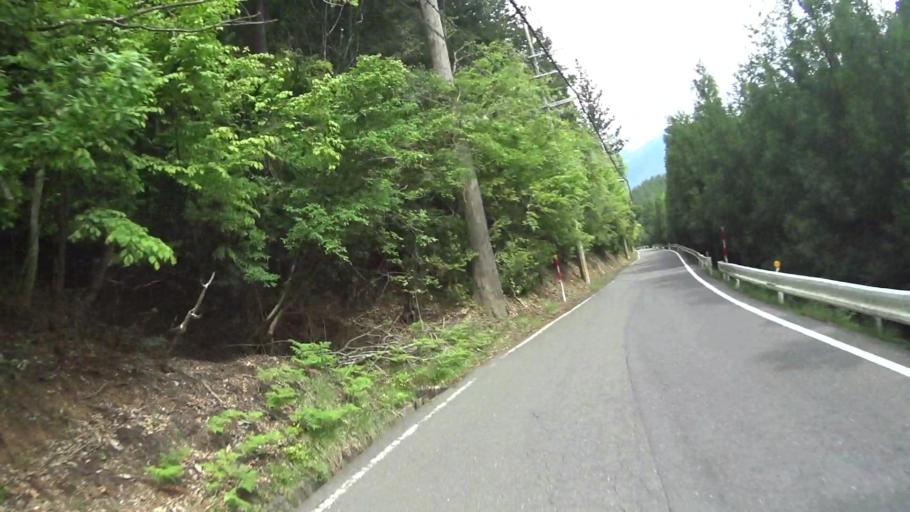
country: JP
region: Kyoto
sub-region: Kyoto-shi
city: Kamigyo-ku
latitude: 35.1872
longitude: 135.6477
